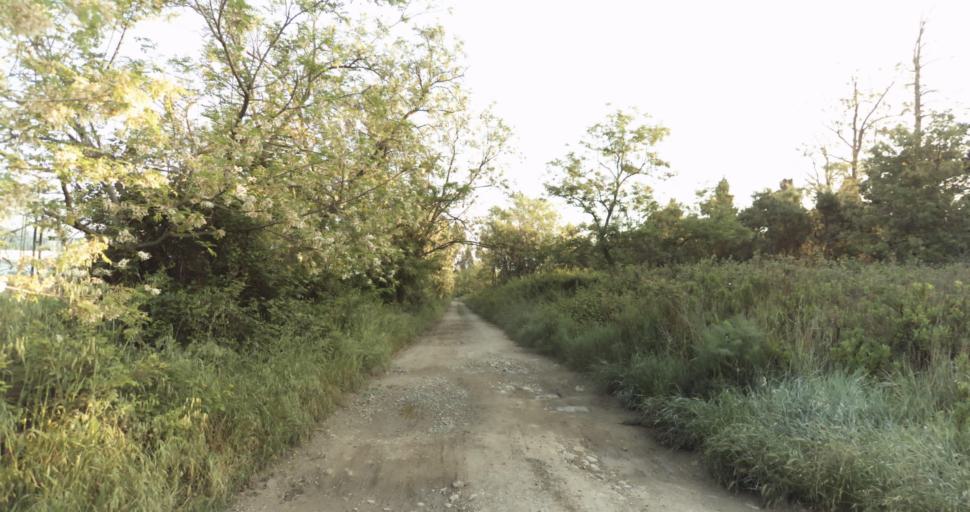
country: FR
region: Corsica
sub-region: Departement de la Haute-Corse
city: Biguglia
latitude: 42.6318
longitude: 9.4406
